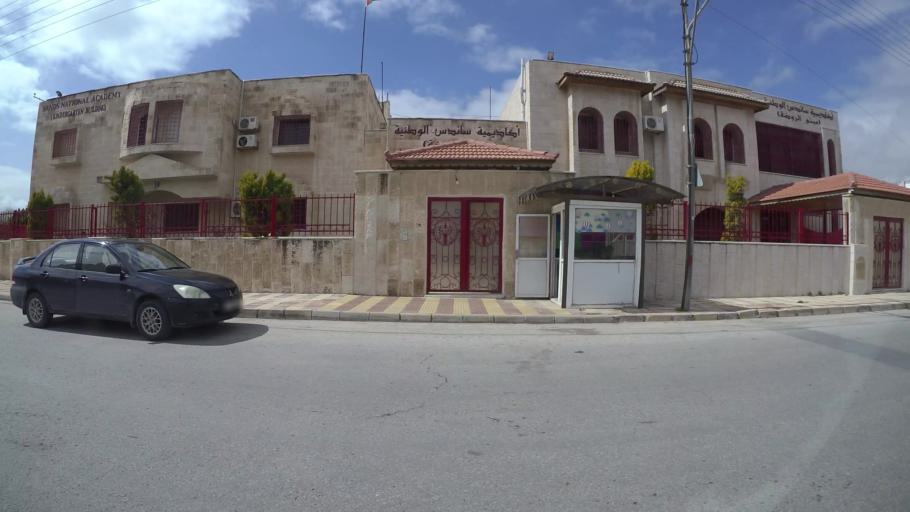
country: JO
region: Amman
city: Al Jubayhah
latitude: 31.9915
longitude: 35.8453
